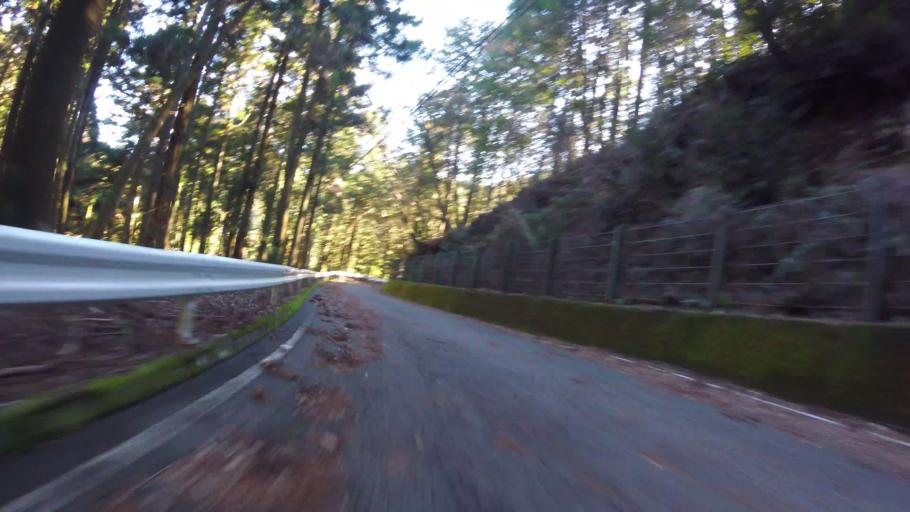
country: JP
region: Shizuoka
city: Ito
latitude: 34.8999
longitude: 138.9572
